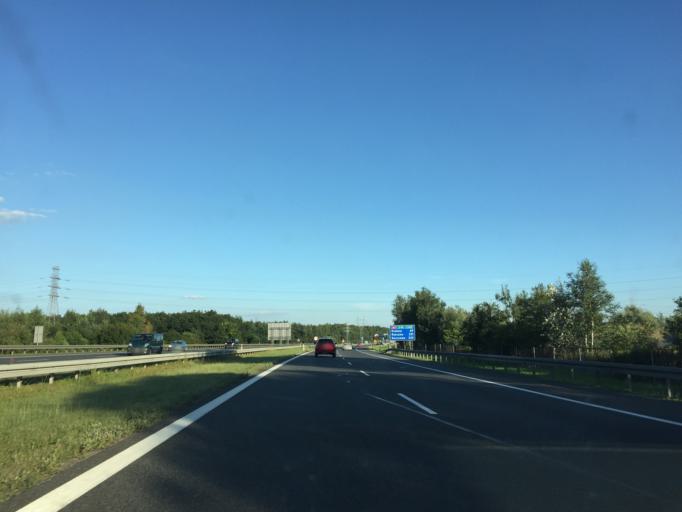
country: PL
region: Silesian Voivodeship
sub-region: Myslowice
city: Myslowice
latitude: 50.2038
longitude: 19.1780
